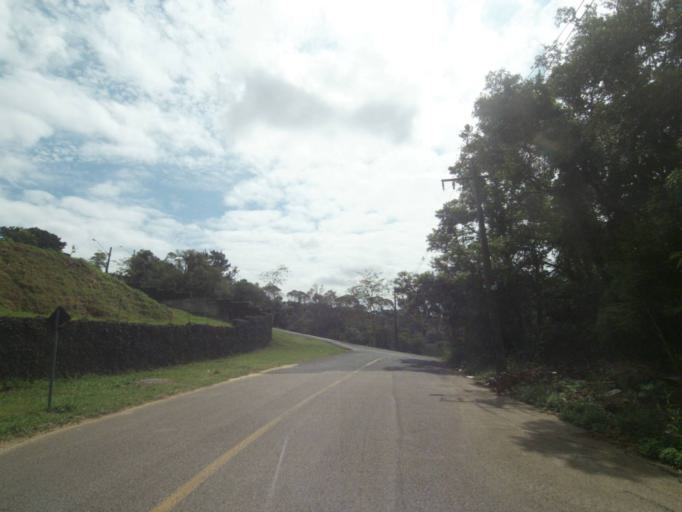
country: BR
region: Parana
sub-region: Curitiba
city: Curitiba
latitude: -25.3815
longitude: -49.2837
